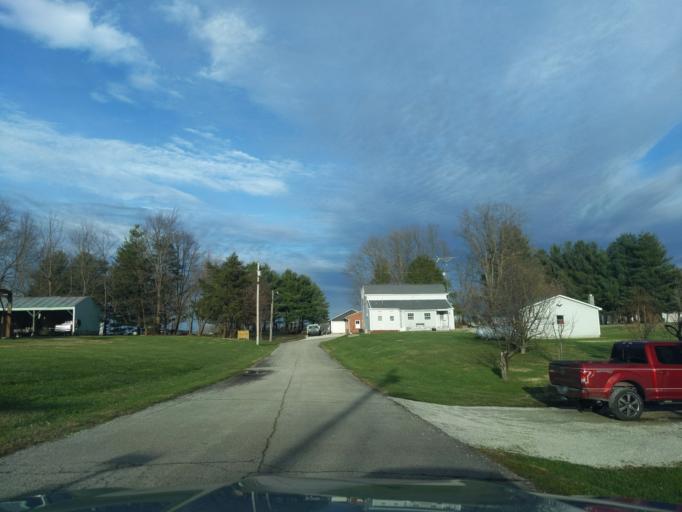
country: US
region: Indiana
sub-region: Decatur County
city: Greensburg
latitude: 39.2112
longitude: -85.4341
